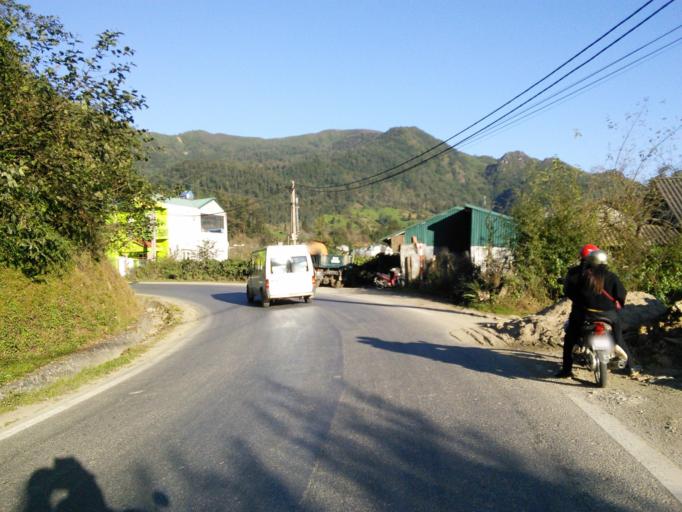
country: VN
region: Lao Cai
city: Sa Pa
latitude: 22.3693
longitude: 103.7963
